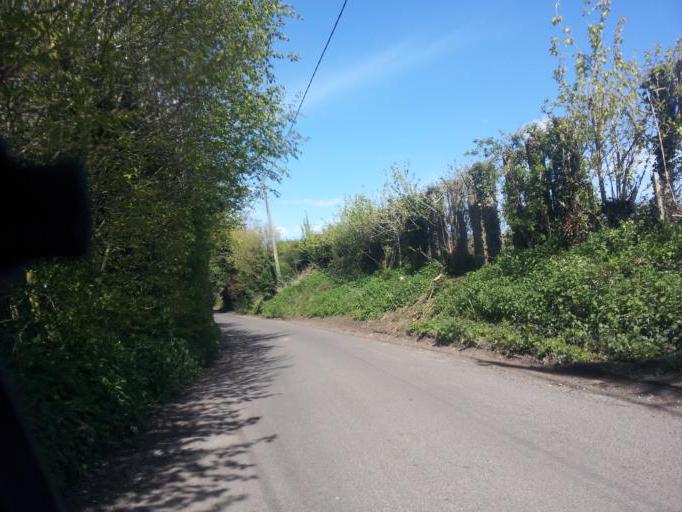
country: GB
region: England
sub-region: Kent
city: Newington
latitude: 51.3394
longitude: 0.6545
